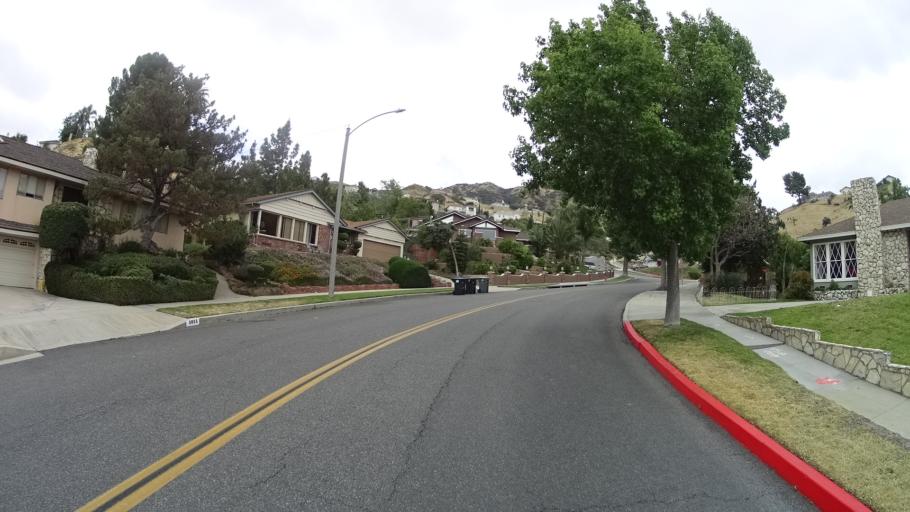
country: US
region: California
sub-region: Los Angeles County
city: Burbank
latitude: 34.2135
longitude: -118.3326
